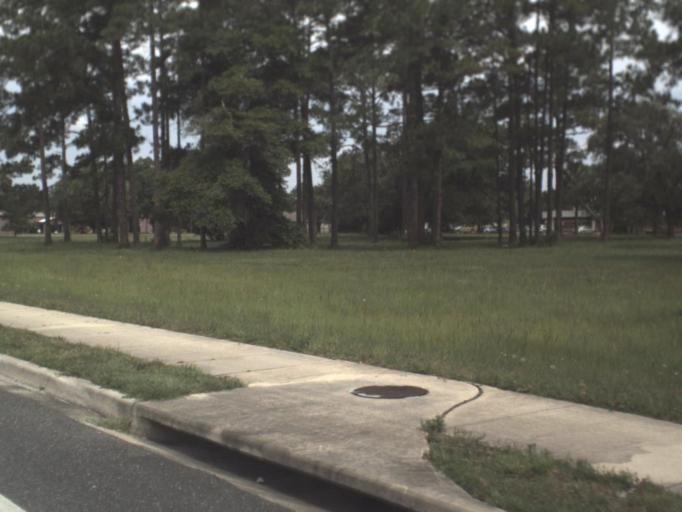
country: US
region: Florida
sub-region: Putnam County
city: Palatka
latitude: 29.6413
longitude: -81.6824
